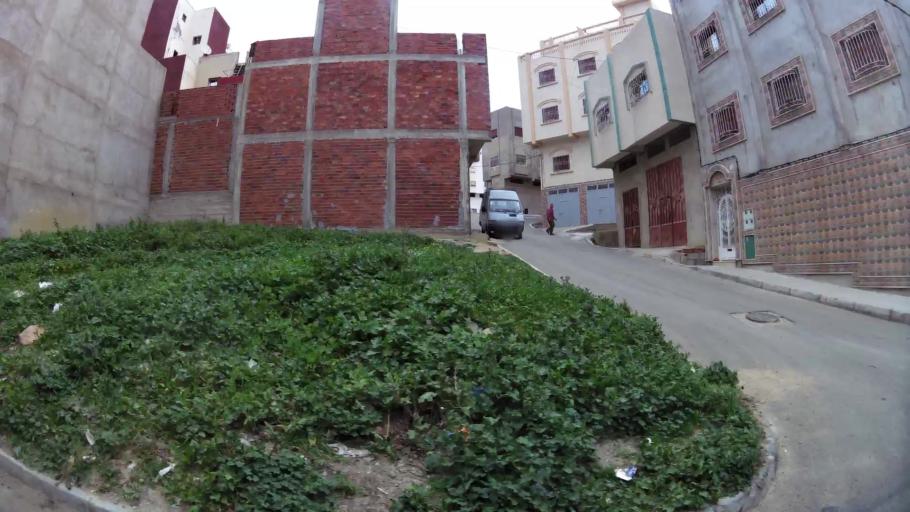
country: MA
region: Tanger-Tetouan
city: Tetouan
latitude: 35.5690
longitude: -5.3926
